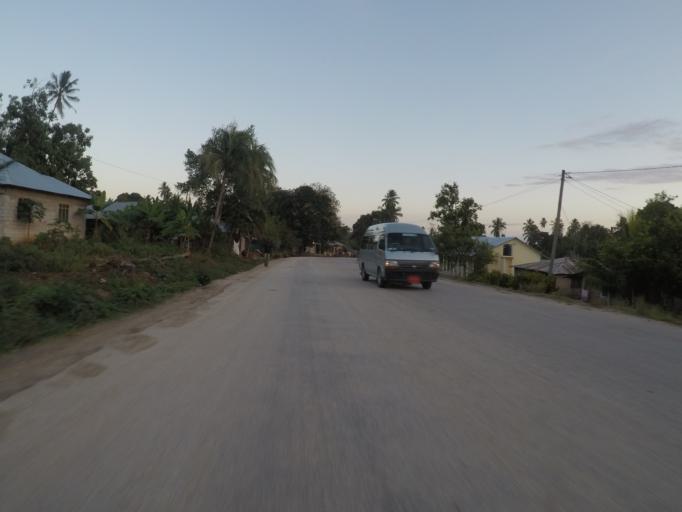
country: TZ
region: Zanzibar North
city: Gamba
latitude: -5.9941
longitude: 39.2526
